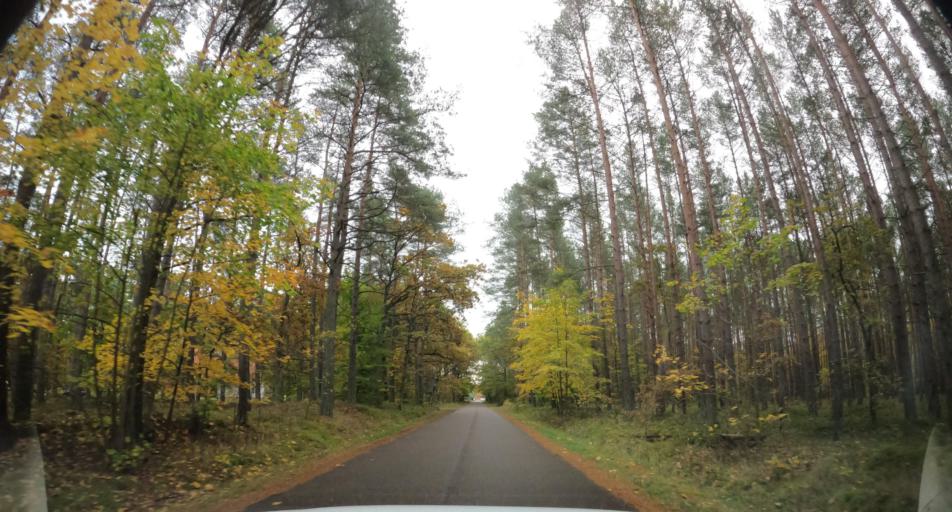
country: PL
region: West Pomeranian Voivodeship
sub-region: Powiat kamienski
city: Wolin
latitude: 53.9110
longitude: 14.5674
